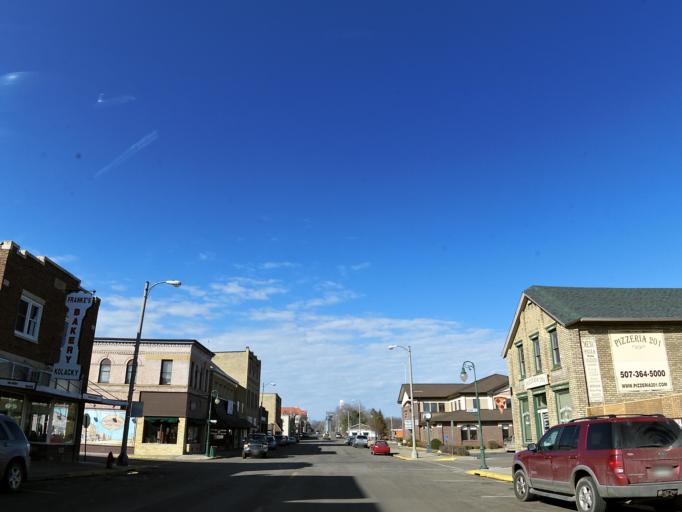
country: US
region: Minnesota
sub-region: Le Sueur County
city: Montgomery
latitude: 44.4374
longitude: -93.5811
